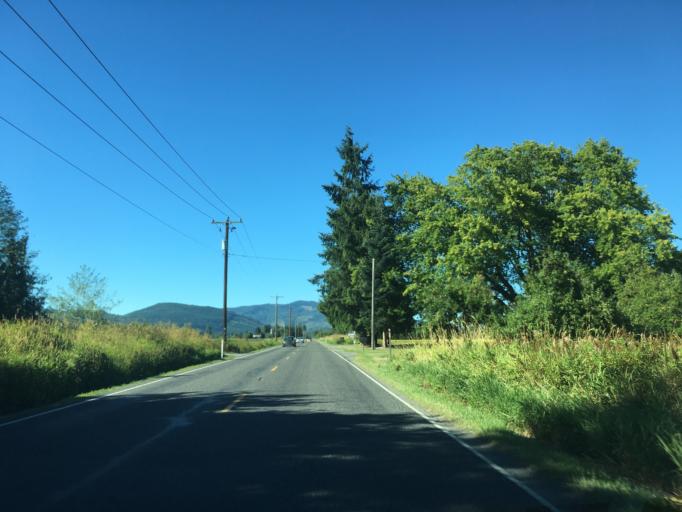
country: US
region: Washington
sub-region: Whatcom County
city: Sudden Valley
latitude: 48.7503
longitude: -122.2021
